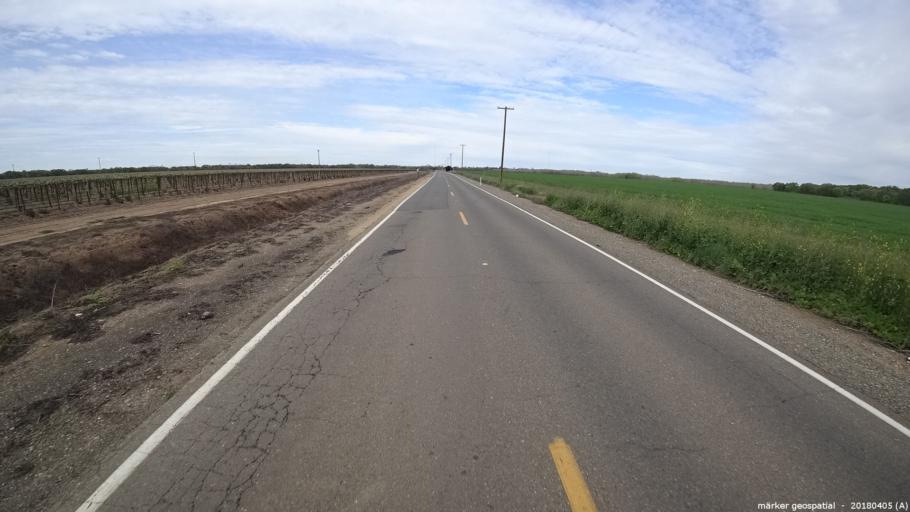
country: US
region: California
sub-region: San Joaquin County
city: Thornton
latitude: 38.2412
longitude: -121.3914
